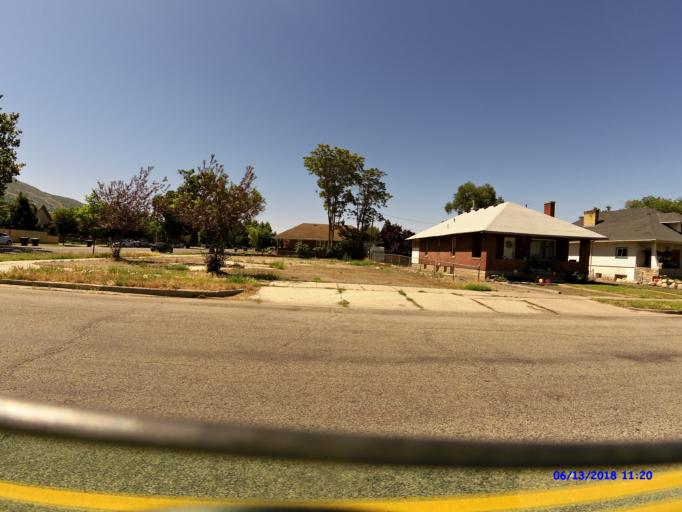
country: US
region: Utah
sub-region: Weber County
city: Ogden
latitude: 41.2205
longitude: -111.9568
